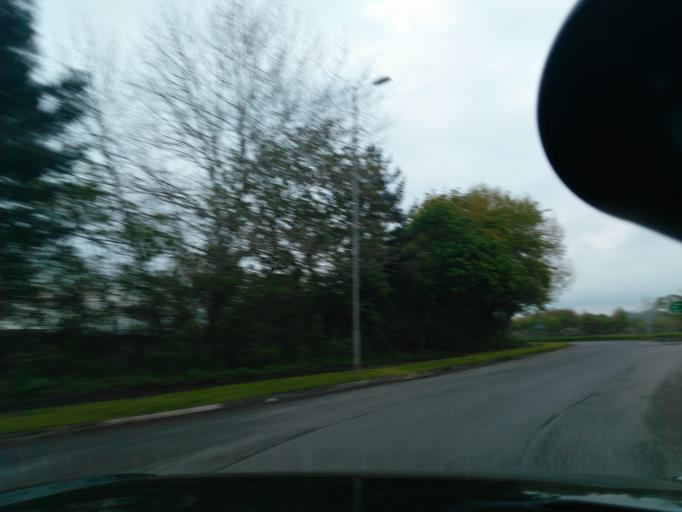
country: GB
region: England
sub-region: Wiltshire
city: Melksham
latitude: 51.3405
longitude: -2.1486
